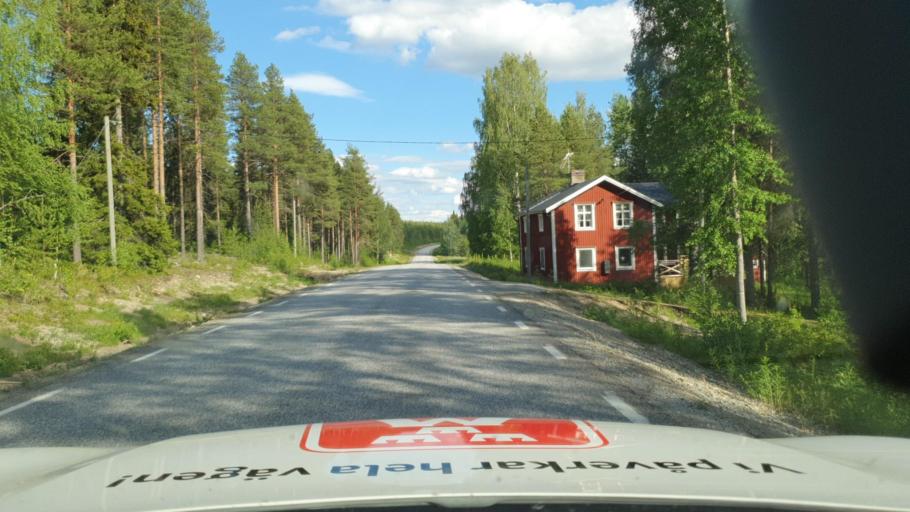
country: SE
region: Vaesterbotten
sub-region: Skelleftea Kommun
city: Langsele
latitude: 64.7242
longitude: 19.9647
